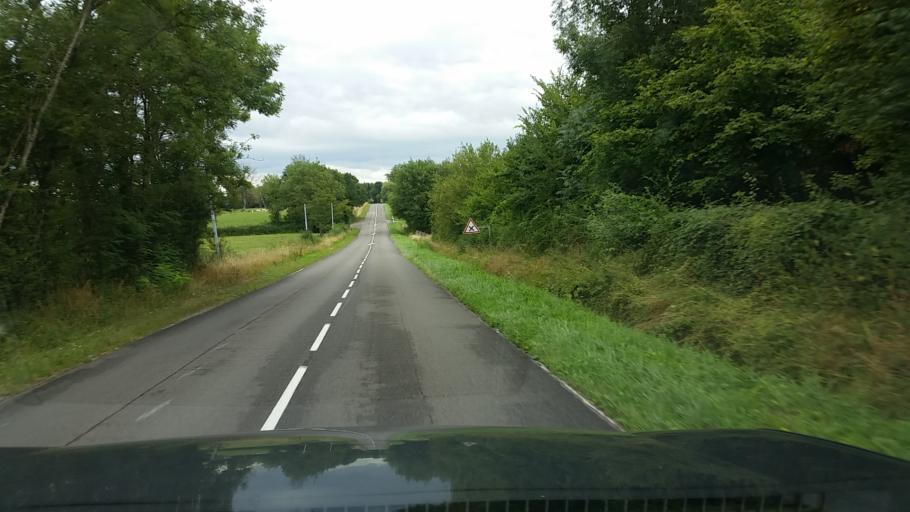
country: FR
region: Bourgogne
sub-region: Departement de Saone-et-Loire
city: Saint-Usuge
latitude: 46.7201
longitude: 5.3051
